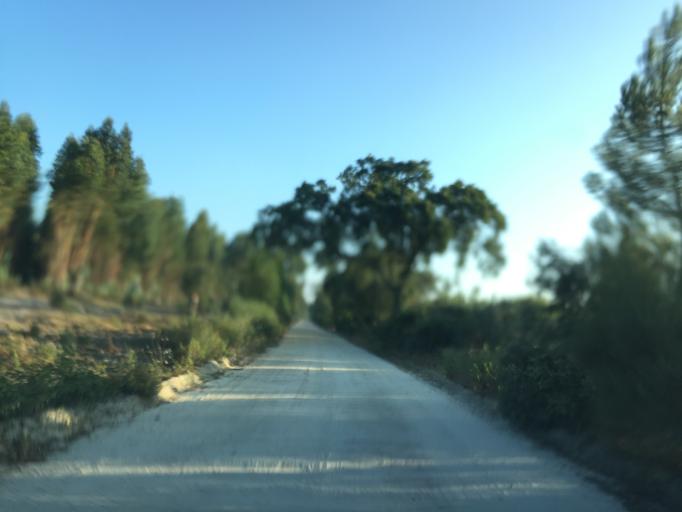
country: PT
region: Portalegre
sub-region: Ponte de Sor
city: Santo Andre
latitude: 39.1507
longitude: -8.3023
